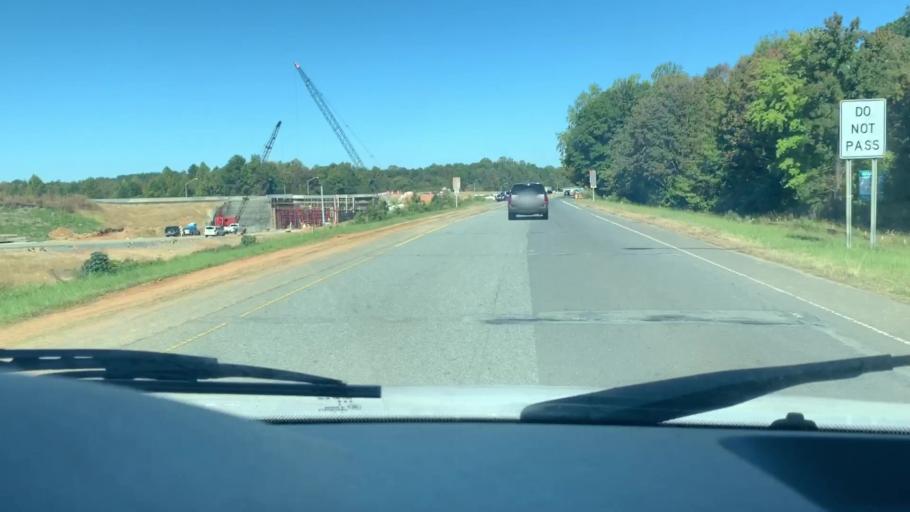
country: US
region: North Carolina
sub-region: Mecklenburg County
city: Charlotte
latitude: 35.2768
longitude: -80.8438
